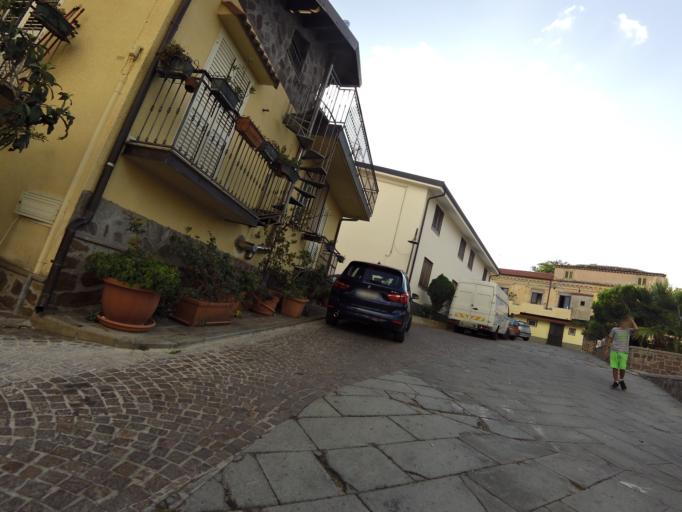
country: IT
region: Calabria
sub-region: Provincia di Reggio Calabria
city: Caulonia
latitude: 38.3830
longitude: 16.4058
